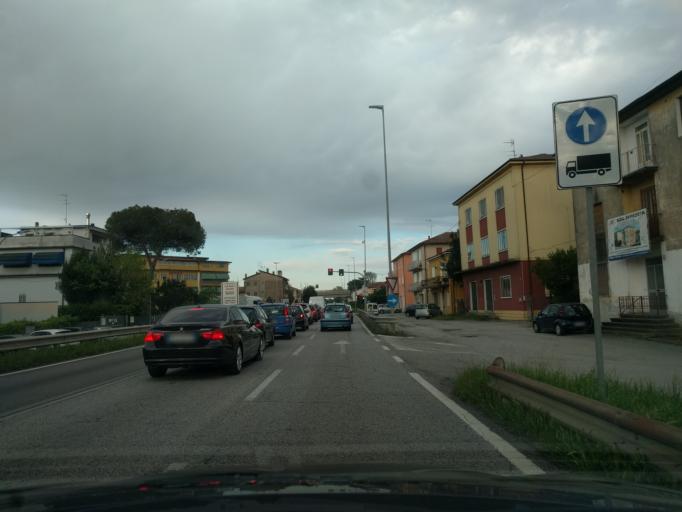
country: IT
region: Veneto
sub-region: Provincia di Rovigo
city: Santa Maria Maddalena
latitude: 44.8914
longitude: 11.6115
